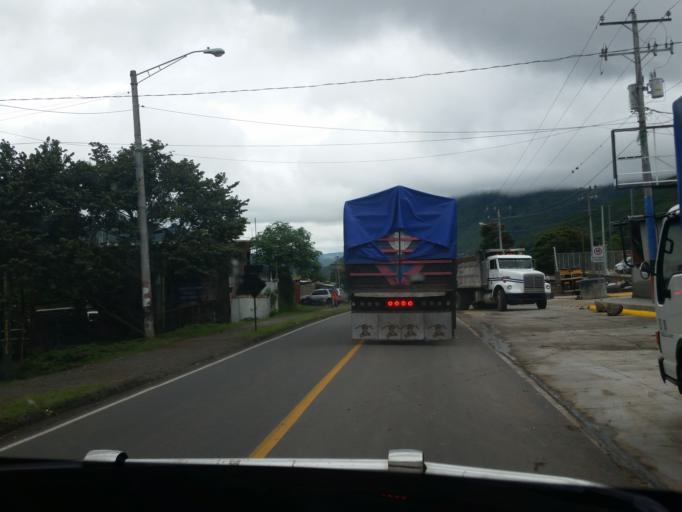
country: NI
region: Jinotega
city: Jinotega
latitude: 13.0836
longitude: -85.9931
